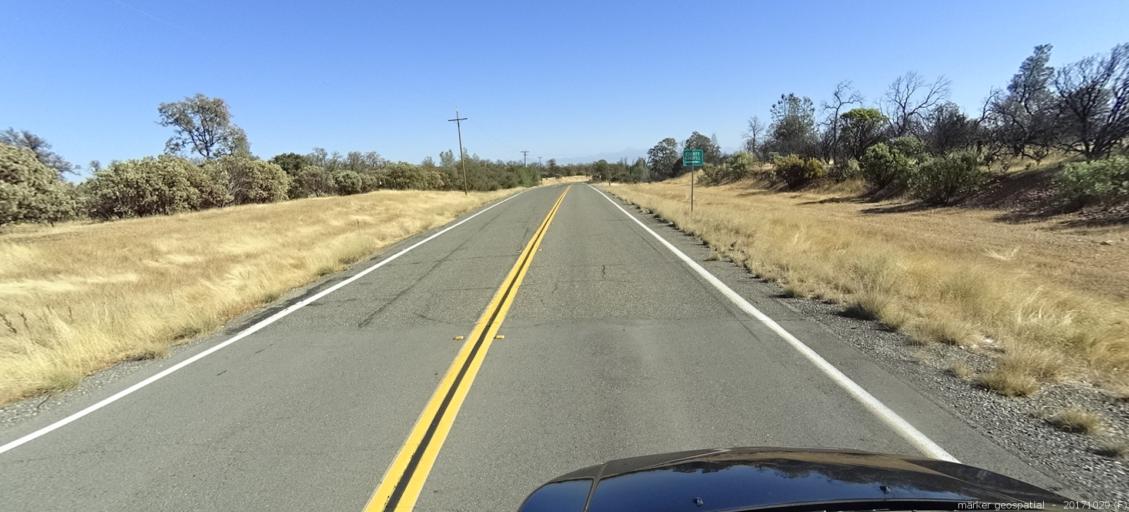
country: US
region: California
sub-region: Shasta County
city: Shasta
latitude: 40.4901
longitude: -122.5412
